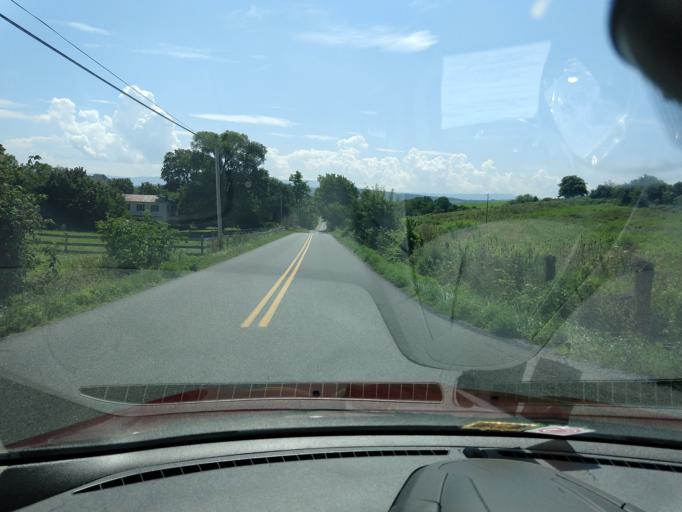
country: US
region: Virginia
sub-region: City of Harrisonburg
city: Harrisonburg
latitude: 38.5329
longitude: -78.8709
